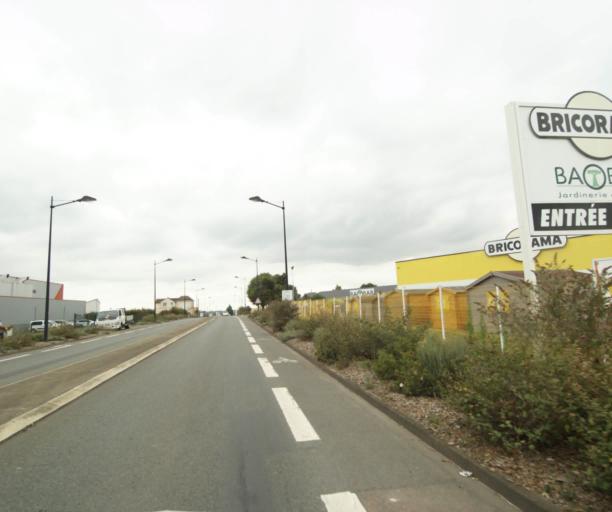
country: FR
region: Pays de la Loire
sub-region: Departement de la Sarthe
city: Sable-sur-Sarthe
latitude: 47.8290
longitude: -0.3106
